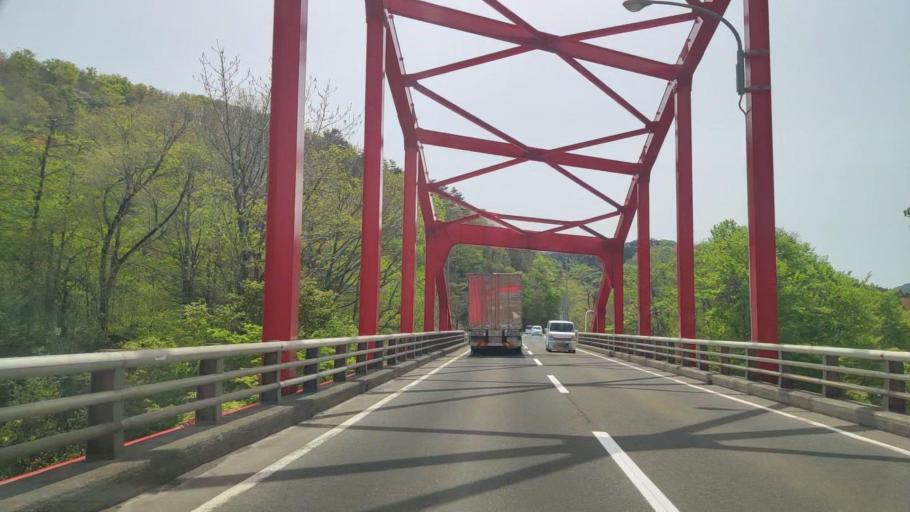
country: JP
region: Aomori
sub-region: Misawa Shi
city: Inuotose
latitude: 40.7897
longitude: 141.0856
